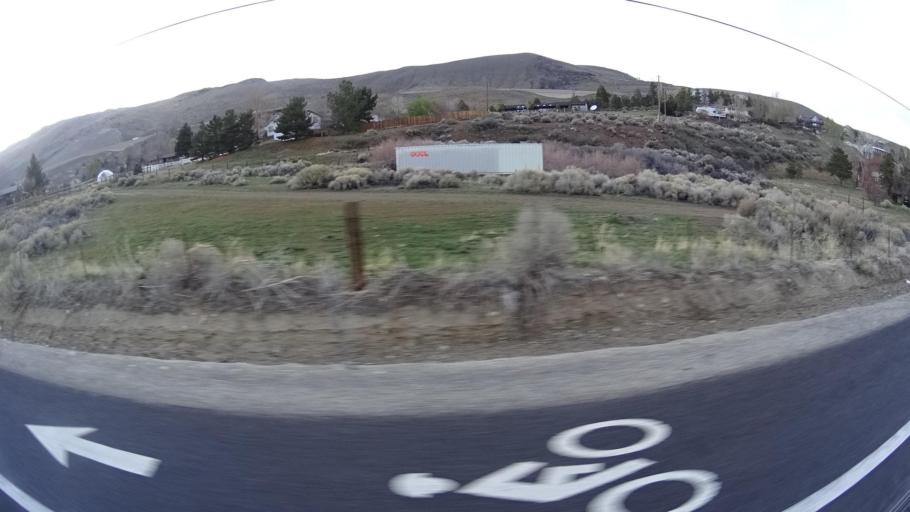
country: US
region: Nevada
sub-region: Storey County
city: Virginia City
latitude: 39.3601
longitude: -119.7660
